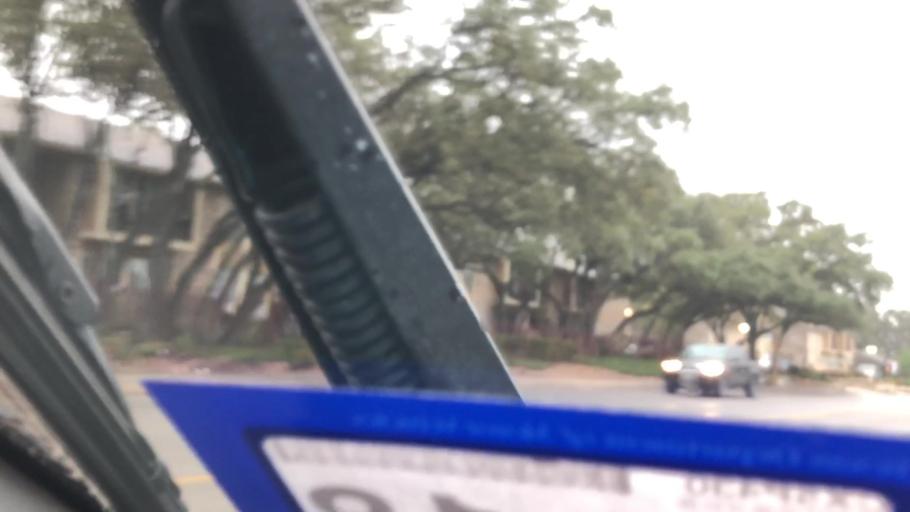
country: US
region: Texas
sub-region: Bexar County
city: Leon Valley
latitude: 29.5007
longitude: -98.5879
